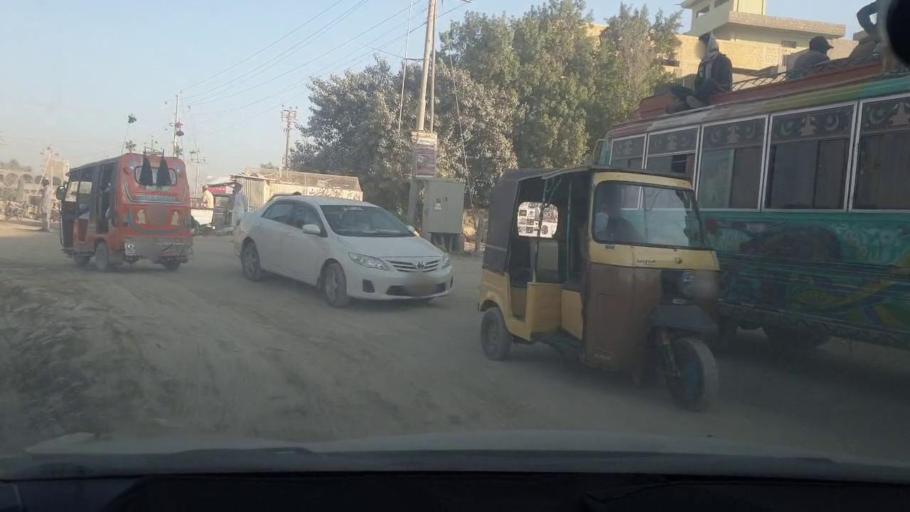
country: PK
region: Sindh
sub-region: Karachi District
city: Karachi
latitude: 24.9752
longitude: 67.0402
